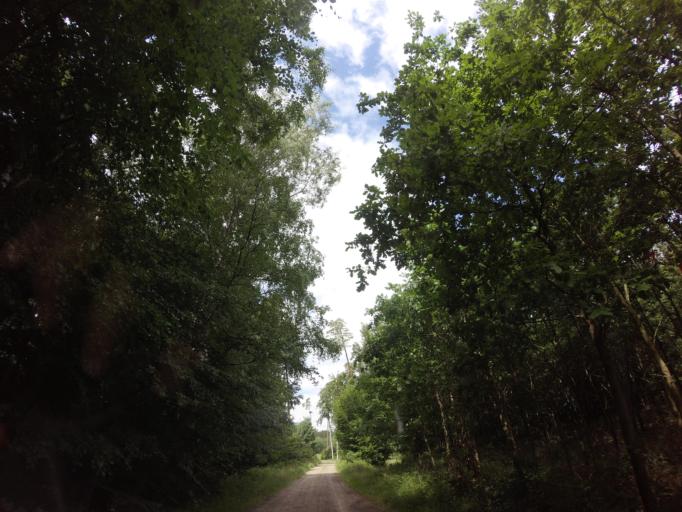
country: PL
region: West Pomeranian Voivodeship
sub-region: Powiat choszczenski
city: Bierzwnik
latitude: 53.0364
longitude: 15.6257
